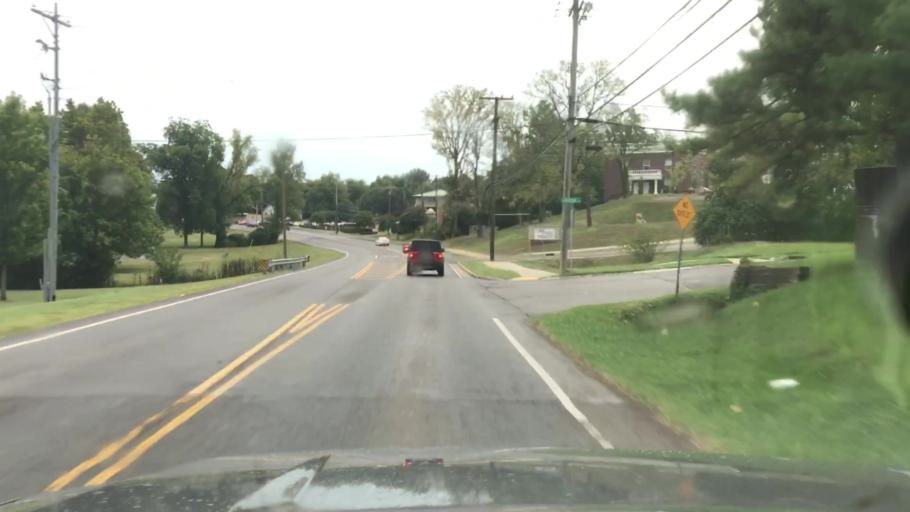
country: US
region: Tennessee
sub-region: Davidson County
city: Lakewood
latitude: 36.1765
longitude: -86.6160
